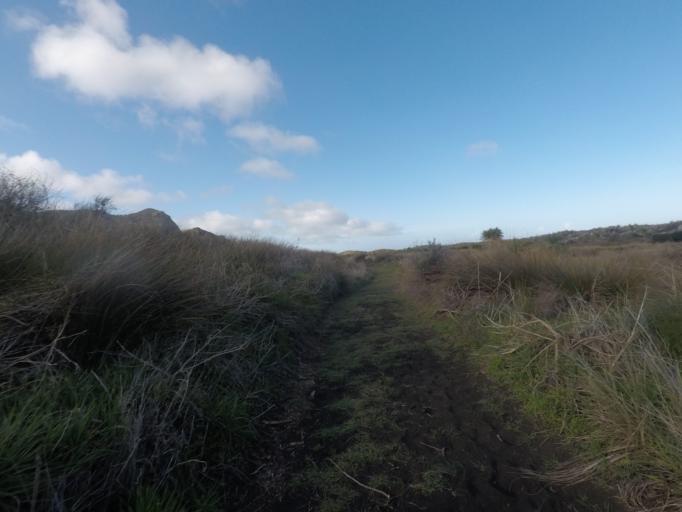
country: NZ
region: Auckland
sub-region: Auckland
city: Titirangi
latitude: -37.0079
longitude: 174.4802
